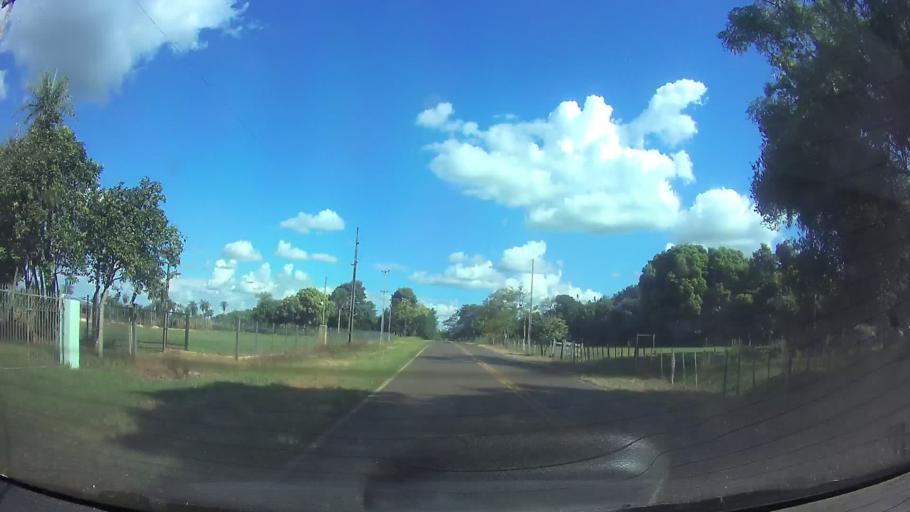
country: PY
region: Paraguari
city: Sapucai
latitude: -25.6543
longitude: -56.8612
